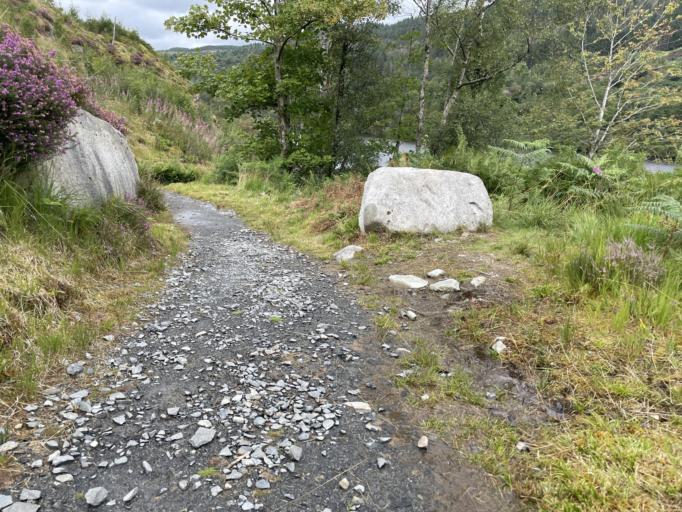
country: GB
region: Scotland
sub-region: Dumfries and Galloway
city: Newton Stewart
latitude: 55.0869
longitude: -4.4869
